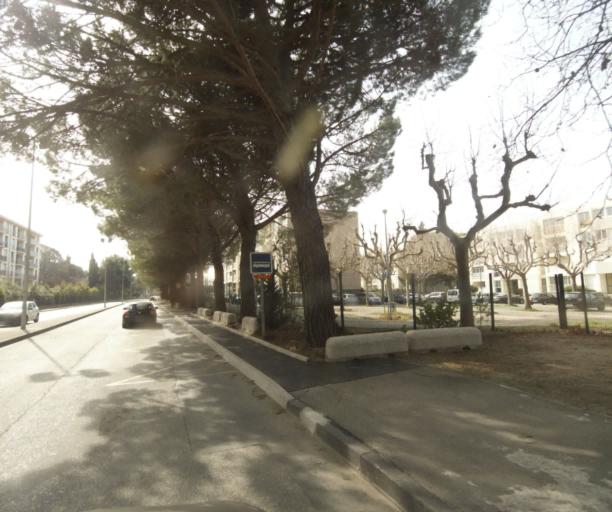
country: FR
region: Provence-Alpes-Cote d'Azur
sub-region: Departement des Bouches-du-Rhone
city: Gardanne
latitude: 43.4561
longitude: 5.4775
